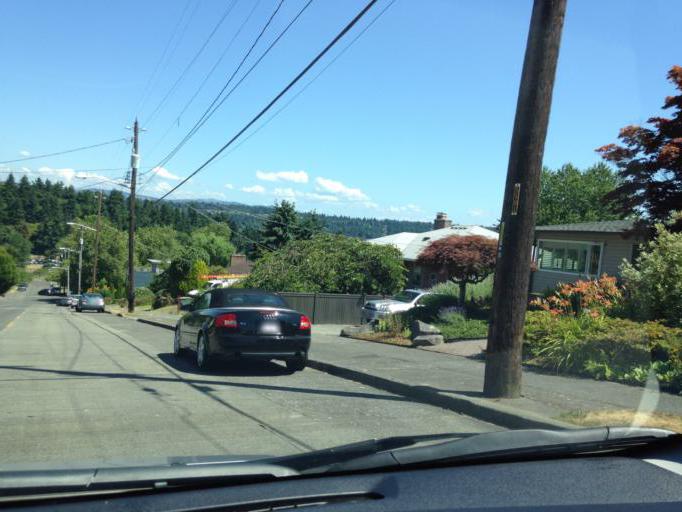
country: US
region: Washington
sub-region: King County
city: Mercer Island
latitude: 47.5511
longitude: -122.2645
